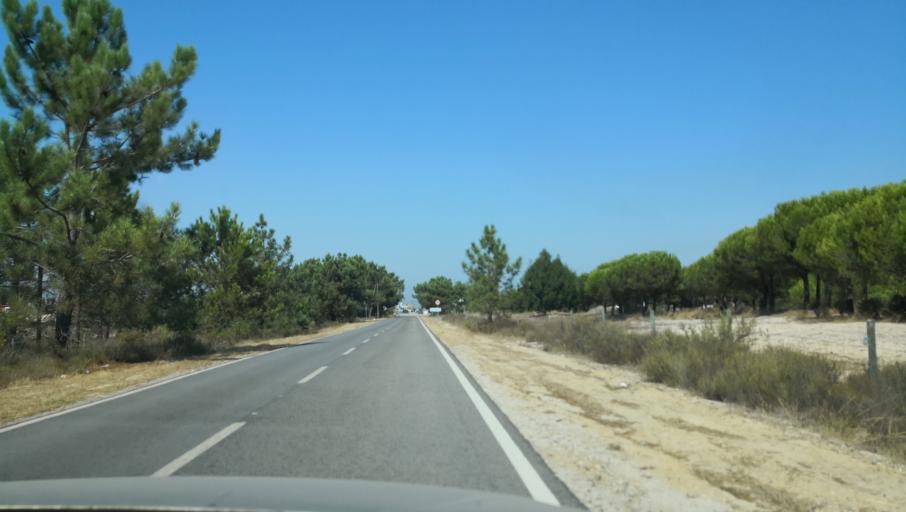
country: PT
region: Setubal
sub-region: Setubal
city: Setubal
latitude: 38.4051
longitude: -8.7461
